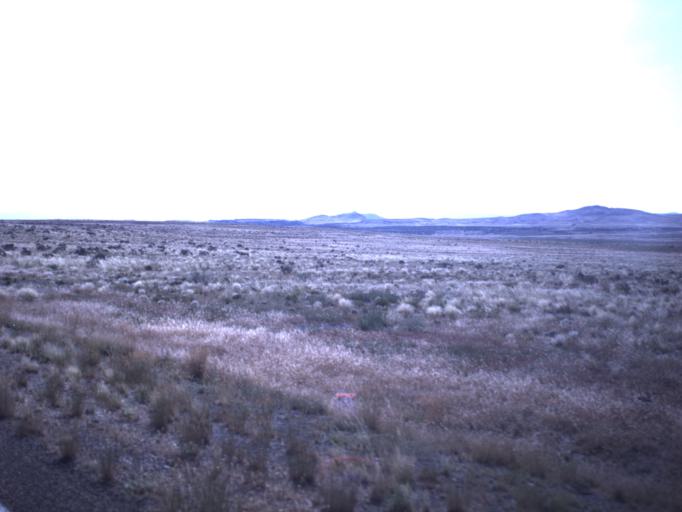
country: US
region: Utah
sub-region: Beaver County
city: Milford
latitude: 38.7980
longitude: -112.8962
